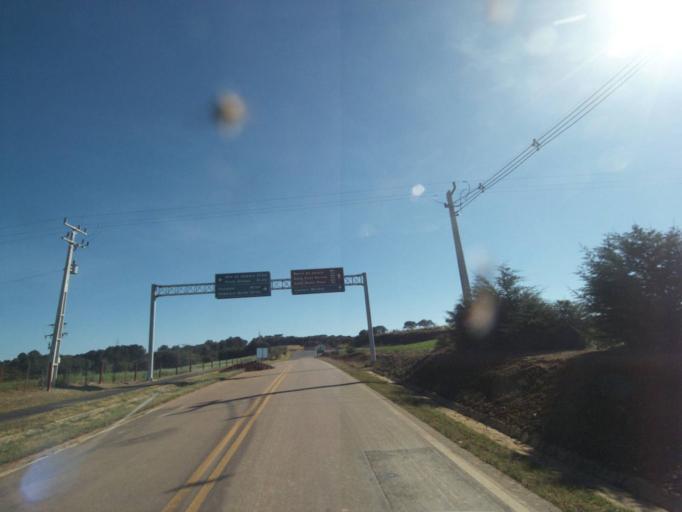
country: BR
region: Parana
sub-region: Tibagi
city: Tibagi
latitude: -24.5266
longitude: -50.4434
